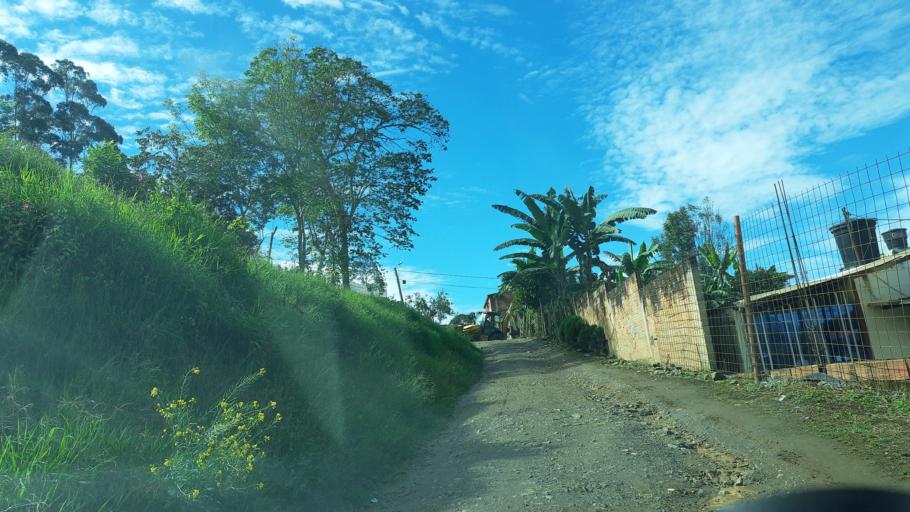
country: CO
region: Boyaca
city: Garagoa
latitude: 5.0843
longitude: -73.3601
